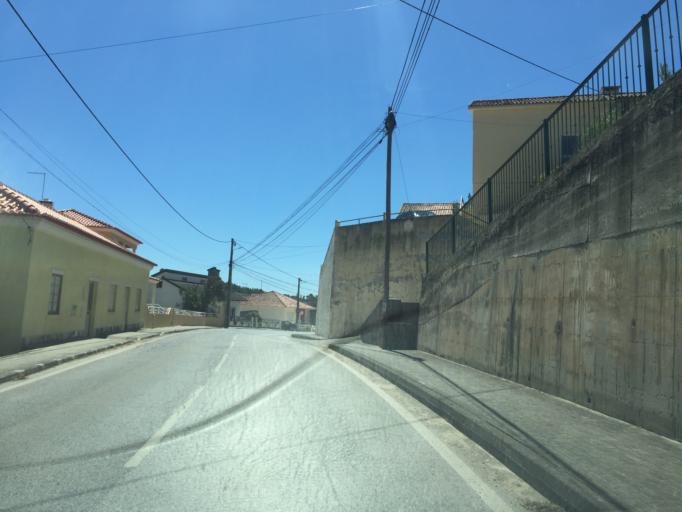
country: PT
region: Lisbon
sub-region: Torres Vedras
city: A dos Cunhados
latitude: 39.1799
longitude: -9.3229
